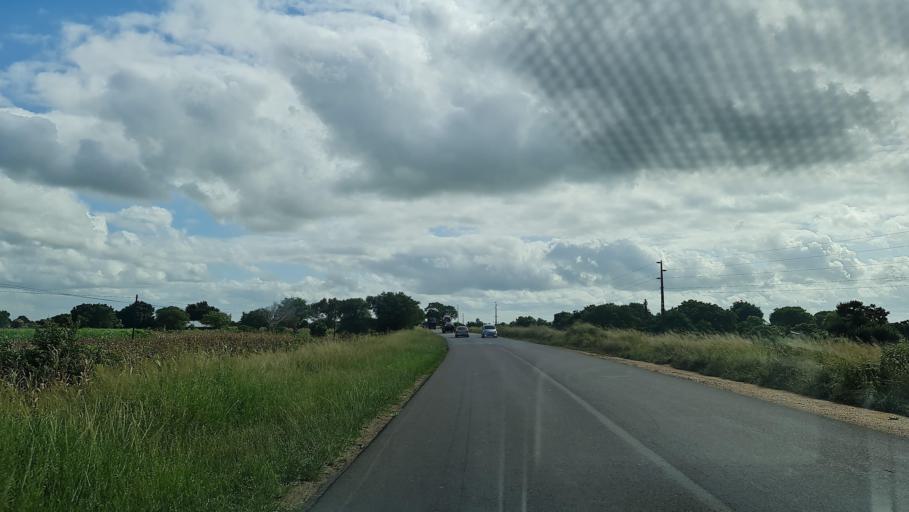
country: MZ
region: Gaza
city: Macia
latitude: -25.0881
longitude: 32.8434
